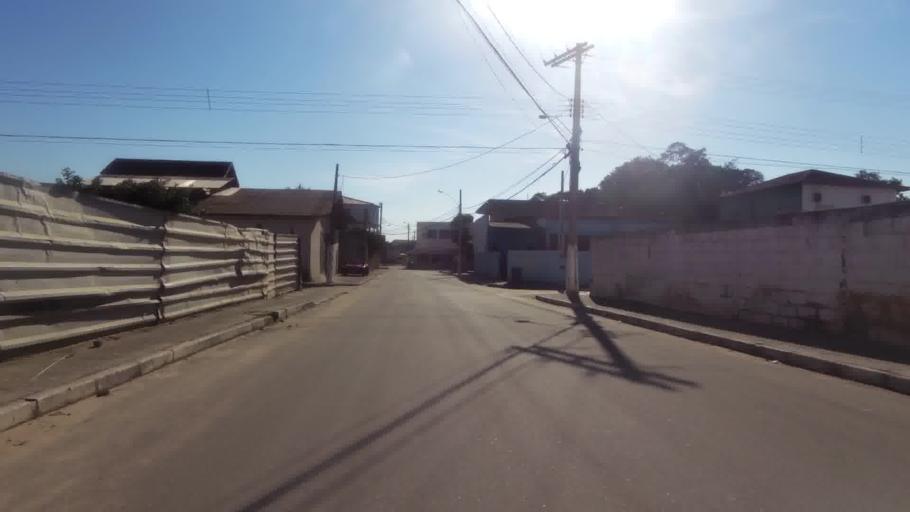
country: BR
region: Espirito Santo
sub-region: Piuma
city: Piuma
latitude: -20.8113
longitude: -40.6343
